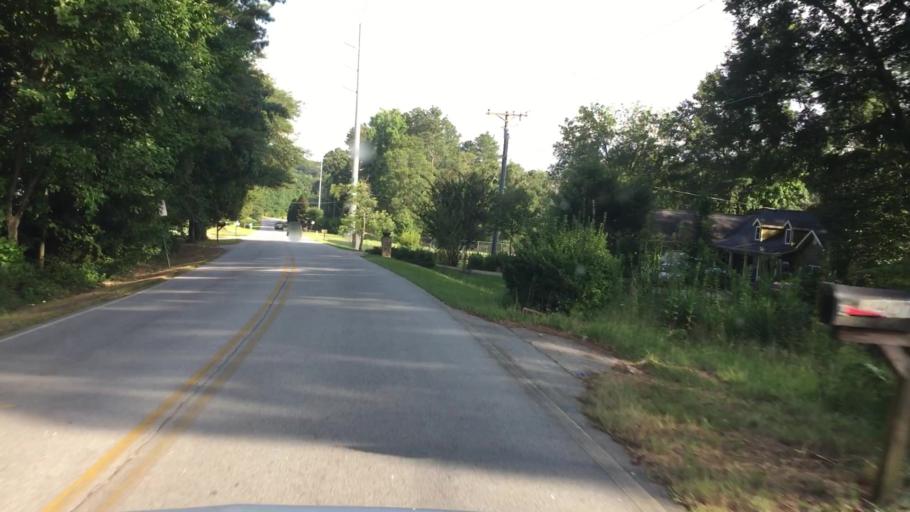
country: US
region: Georgia
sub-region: DeKalb County
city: Pine Mountain
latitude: 33.6355
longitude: -84.1295
